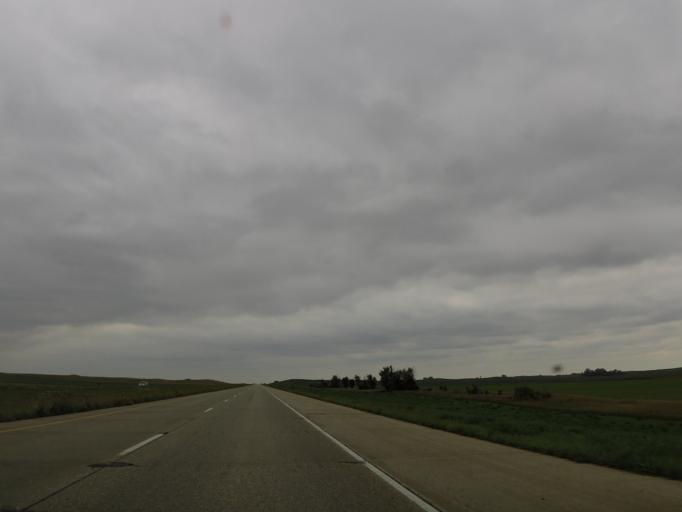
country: US
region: South Dakota
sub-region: Roberts County
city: Sisseton
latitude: 45.6265
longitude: -96.9892
